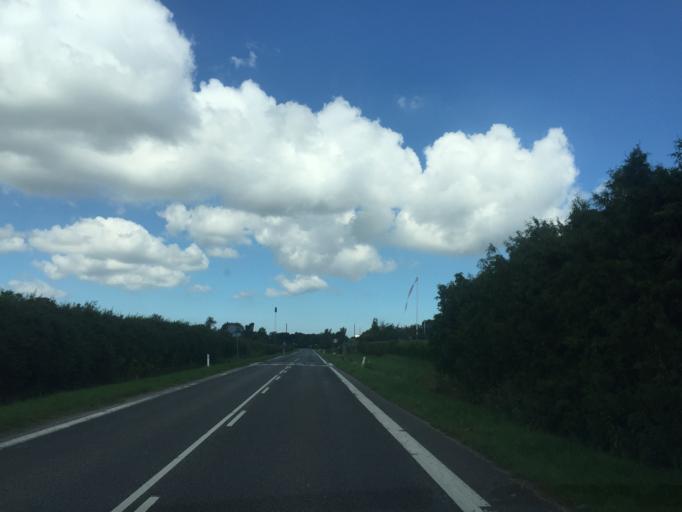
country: DK
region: South Denmark
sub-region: Nordfyns Kommune
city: Otterup
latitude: 55.5216
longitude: 10.3993
